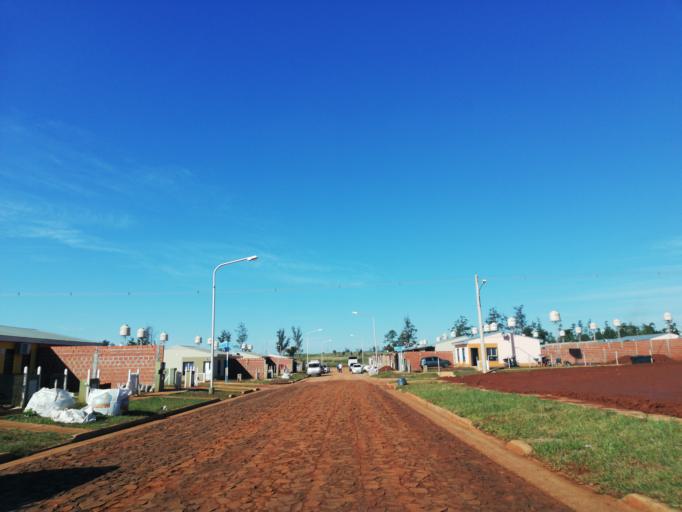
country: AR
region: Misiones
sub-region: Departamento de Capital
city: Posadas
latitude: -27.4162
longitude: -55.9902
